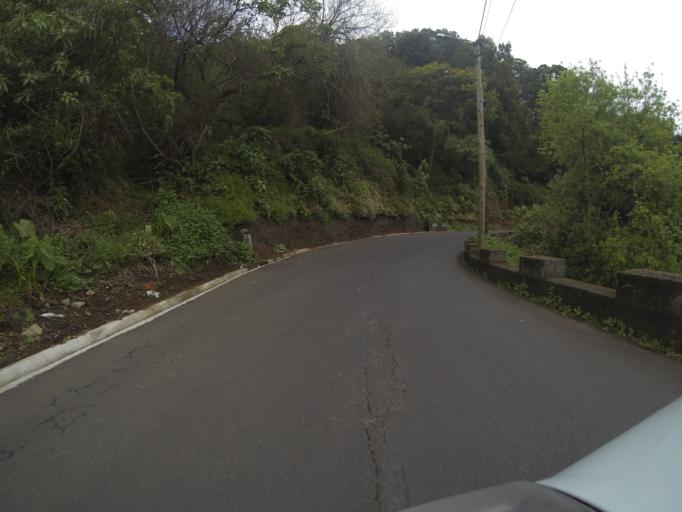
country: PT
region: Madeira
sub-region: Santa Cruz
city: Santa Cruz
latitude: 32.7360
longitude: -16.8095
